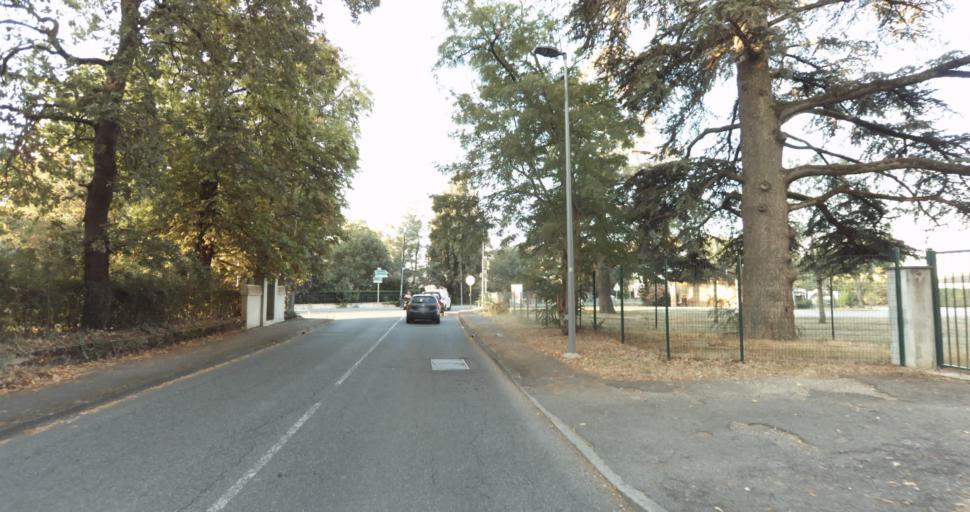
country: FR
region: Midi-Pyrenees
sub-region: Departement de la Haute-Garonne
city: L'Union
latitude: 43.6601
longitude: 1.4885
